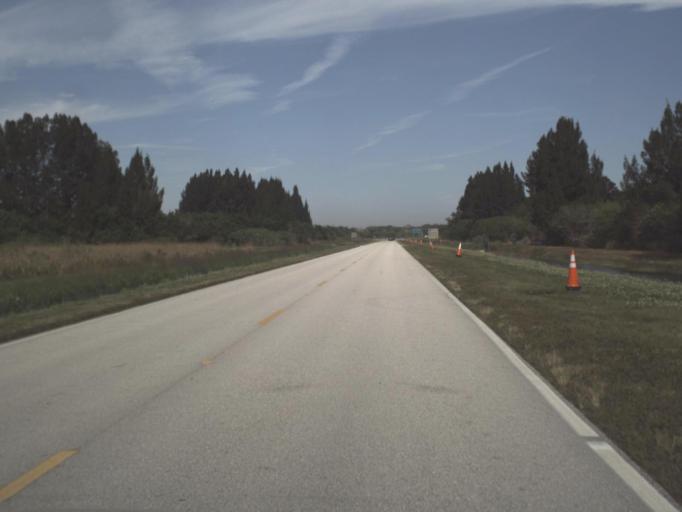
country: US
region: Florida
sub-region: Brevard County
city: Merritt Island
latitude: 28.5059
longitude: -80.6756
